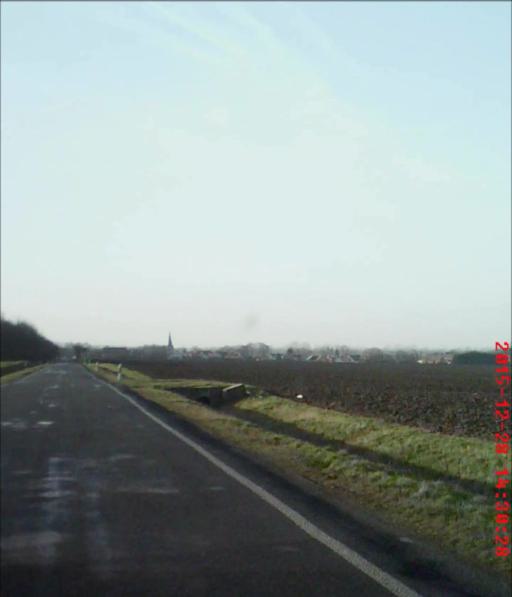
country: DE
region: Thuringia
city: Liebstedt
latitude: 51.0449
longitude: 11.3860
